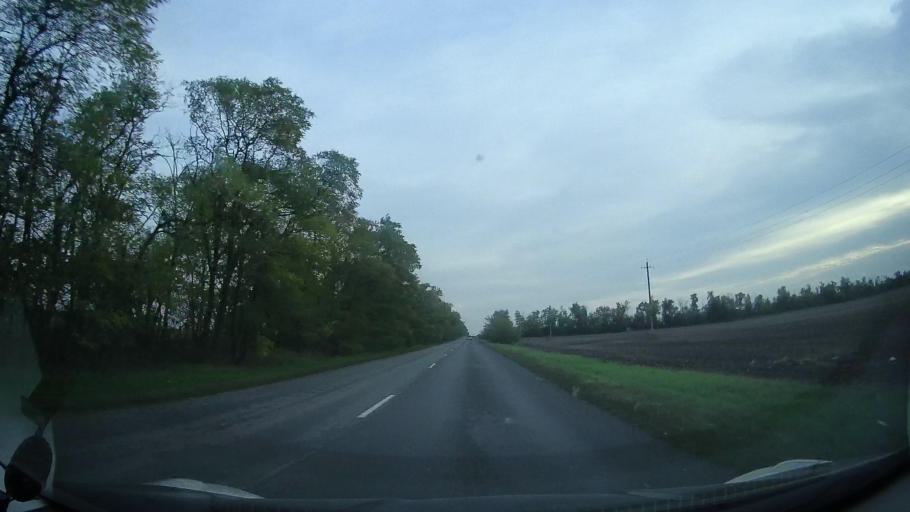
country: RU
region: Rostov
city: Ol'ginskaya
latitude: 47.1012
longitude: 39.9775
